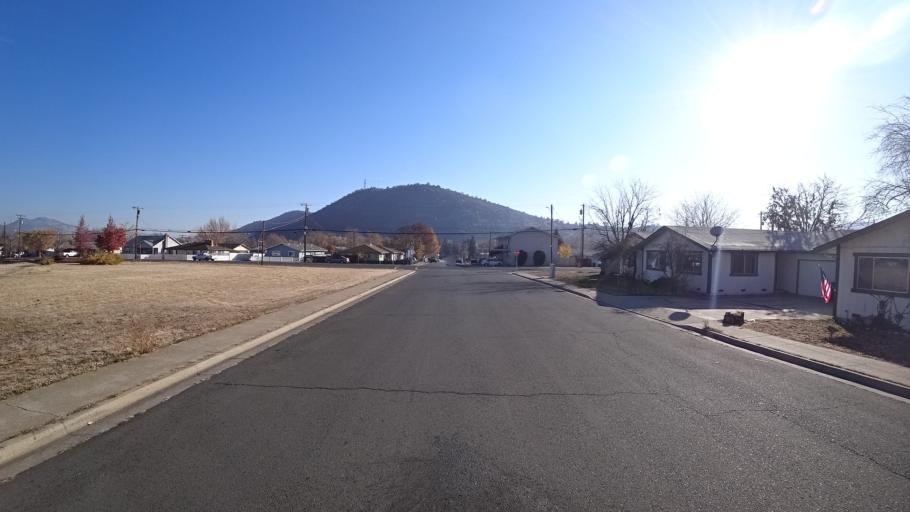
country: US
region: California
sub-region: Siskiyou County
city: Yreka
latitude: 41.7231
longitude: -122.6422
